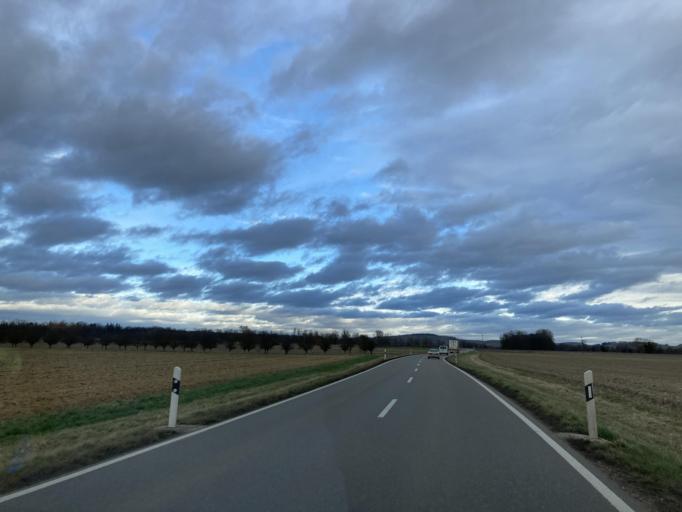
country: DE
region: Baden-Wuerttemberg
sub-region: Freiburg Region
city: Breisach am Rhein
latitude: 48.0584
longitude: 7.5938
